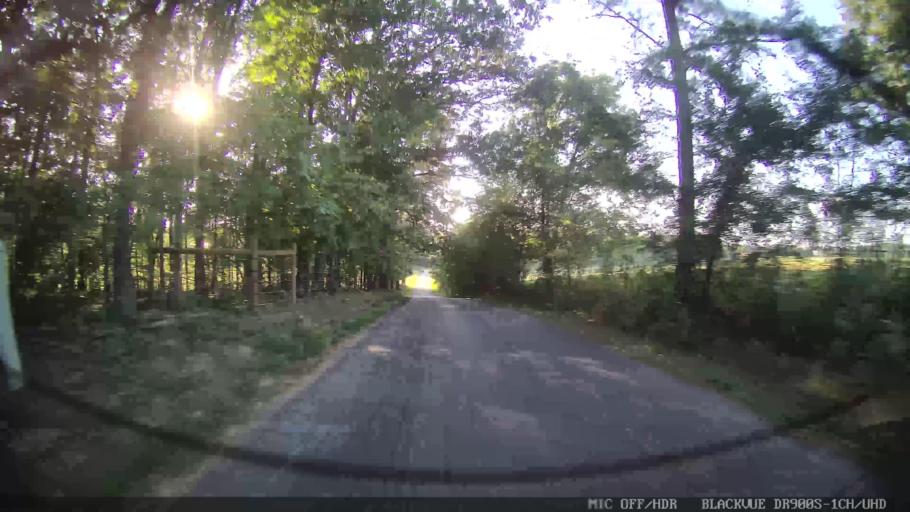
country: US
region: Tennessee
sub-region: Bradley County
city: Wildwood Lake
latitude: 35.0150
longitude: -84.7499
